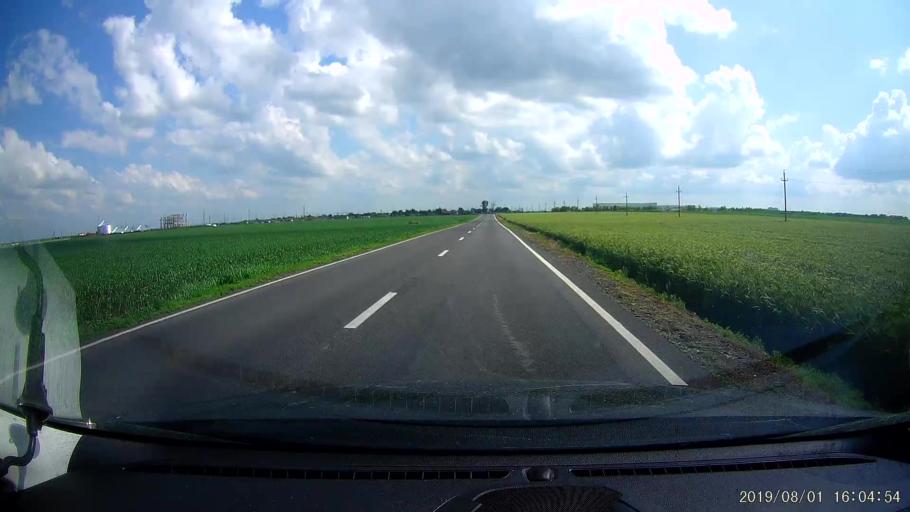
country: RO
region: Calarasi
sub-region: Comuna Dragalina
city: Drajna Noua
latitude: 44.4357
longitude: 27.3780
